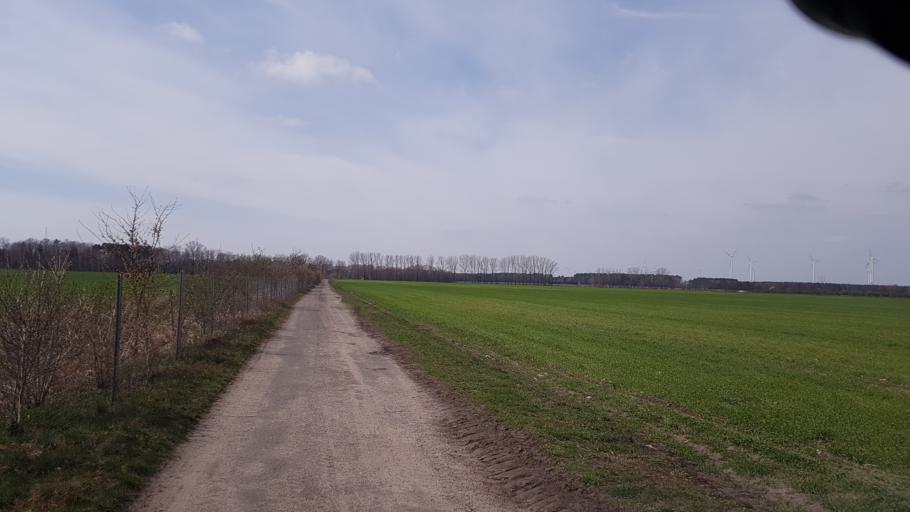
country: DE
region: Brandenburg
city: Bronkow
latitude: 51.6377
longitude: 13.9192
